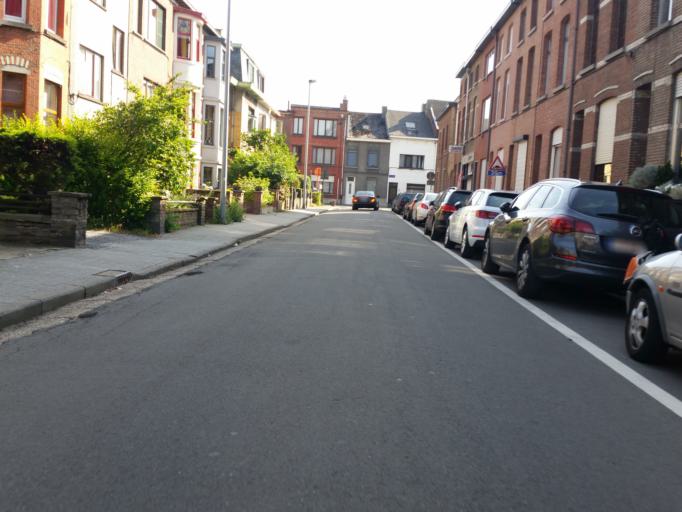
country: BE
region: Flanders
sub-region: Provincie Antwerpen
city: Mechelen
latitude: 51.0356
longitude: 4.4873
